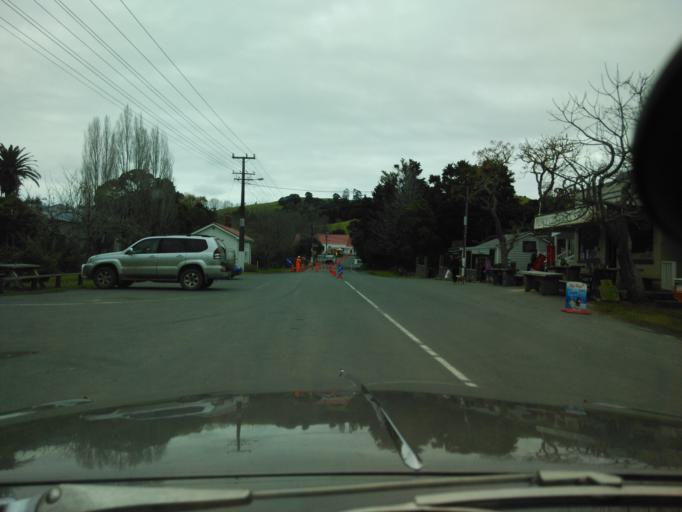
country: NZ
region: Auckland
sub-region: Auckland
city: Warkworth
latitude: -36.5120
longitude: 174.6612
